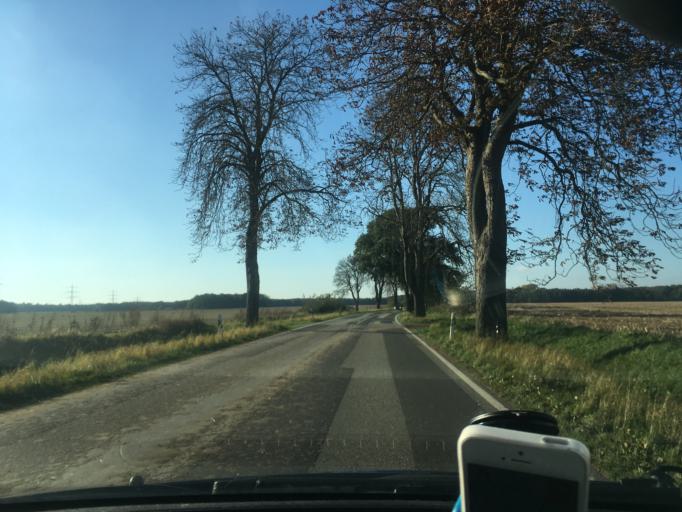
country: DE
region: Mecklenburg-Vorpommern
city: Wittenburg
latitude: 53.5209
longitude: 10.9998
